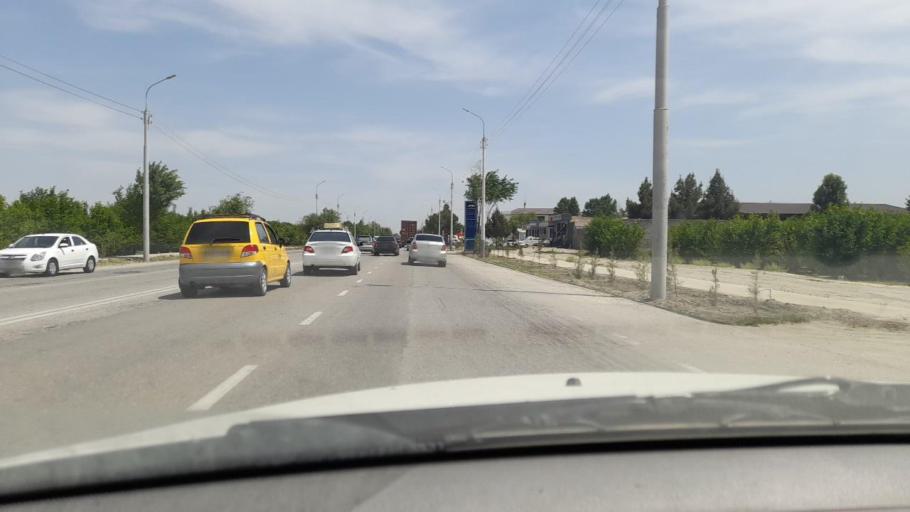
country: UZ
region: Navoiy
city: Karmana Shahri
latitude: 40.1472
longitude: 65.3304
